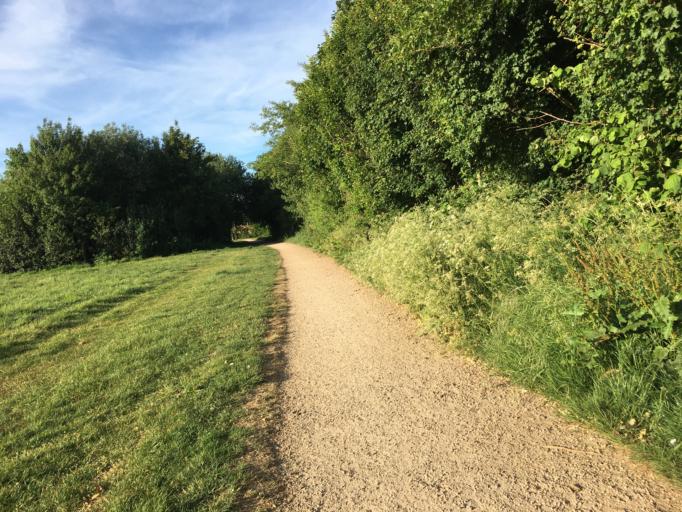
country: GB
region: England
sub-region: Warwickshire
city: Rugby
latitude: 52.3606
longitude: -1.2259
